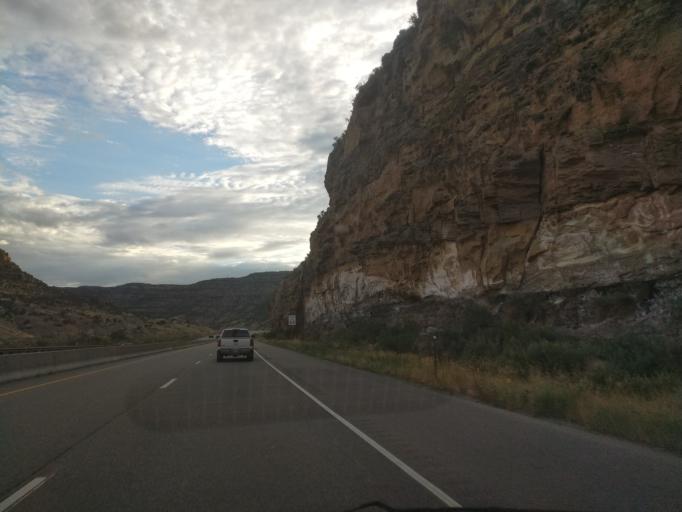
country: US
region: Colorado
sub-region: Mesa County
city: Palisade
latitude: 39.2042
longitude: -108.2646
